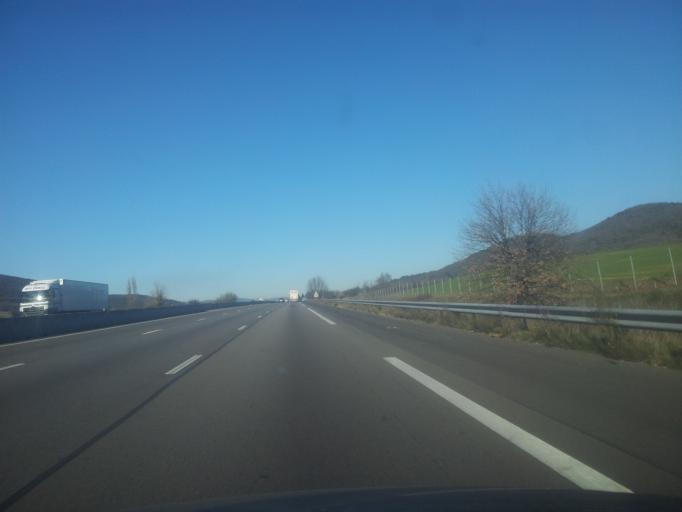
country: FR
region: Rhone-Alpes
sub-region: Departement de la Drome
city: Savasse
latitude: 44.6159
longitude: 4.7930
